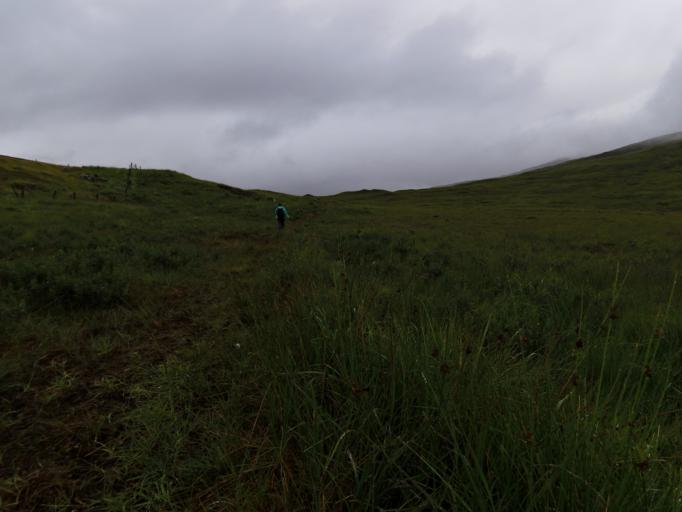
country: GB
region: Scotland
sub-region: Highland
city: Spean Bridge
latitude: 56.7709
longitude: -4.7086
